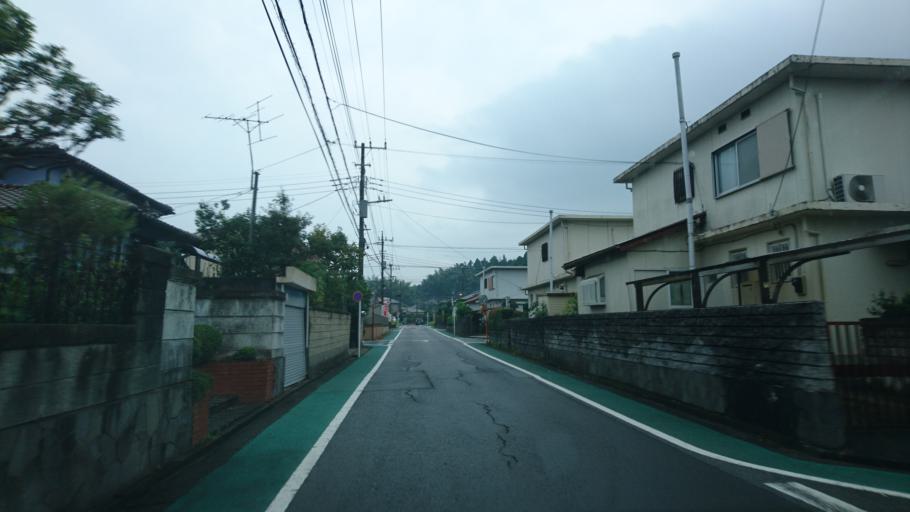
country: JP
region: Chiba
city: Kimitsu
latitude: 35.3034
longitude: 139.9565
